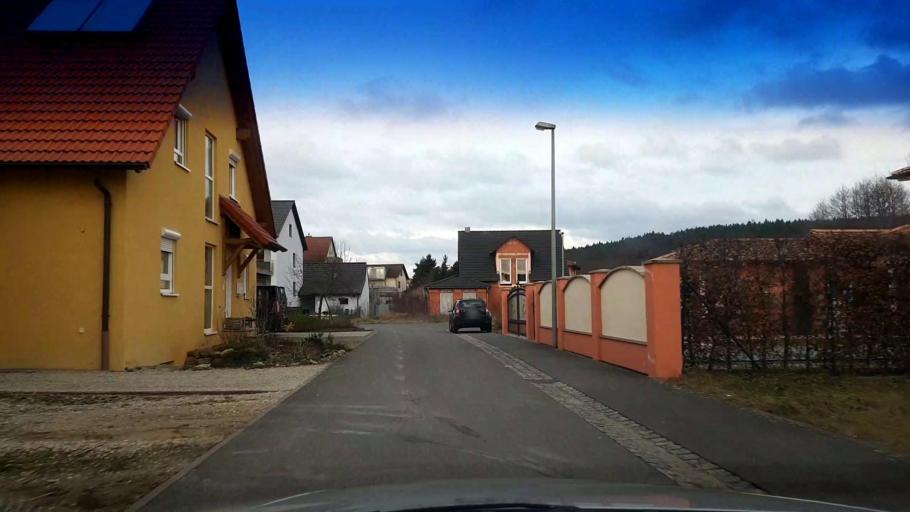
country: DE
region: Bavaria
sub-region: Upper Franconia
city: Gundelsheim
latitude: 49.9360
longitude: 10.9278
